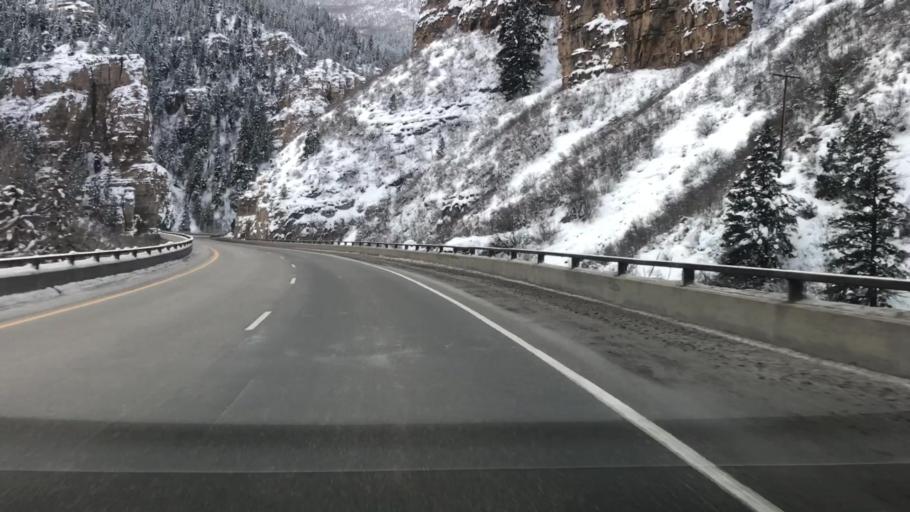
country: US
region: Colorado
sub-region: Garfield County
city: Glenwood Springs
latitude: 39.6075
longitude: -107.1558
